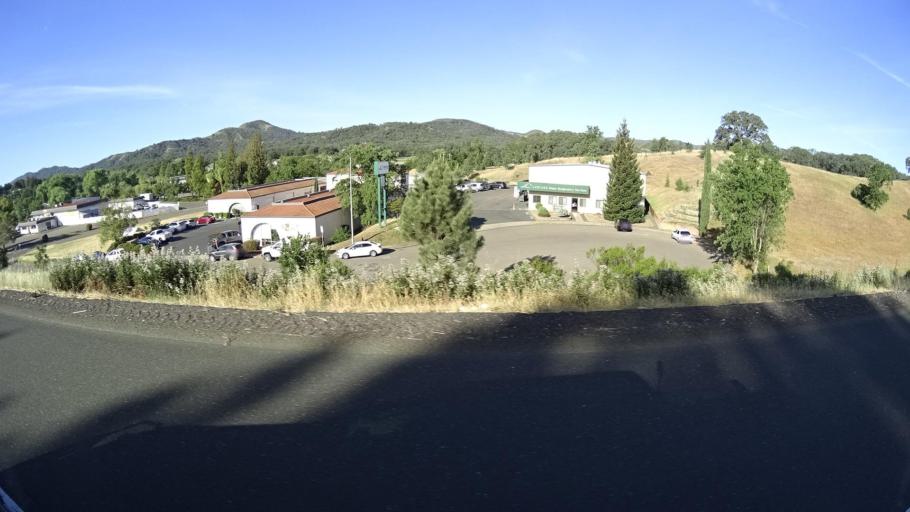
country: US
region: California
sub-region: Lake County
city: Lakeport
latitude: 39.0383
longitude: -122.9283
